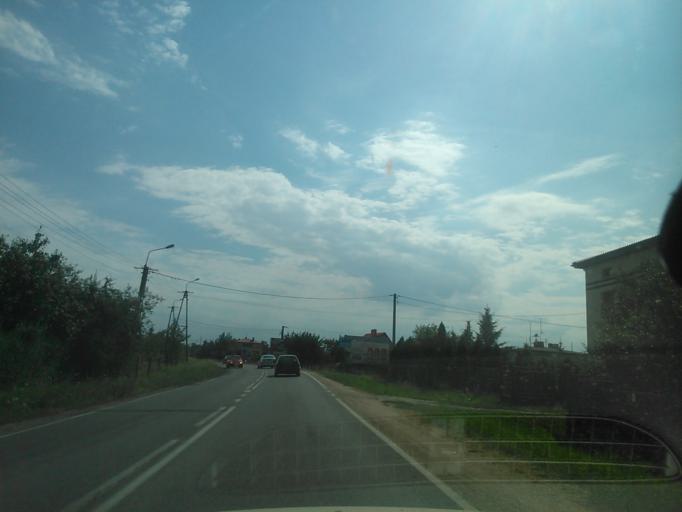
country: PL
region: Masovian Voivodeship
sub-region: Powiat mlawski
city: Mlawa
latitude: 53.1331
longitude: 20.3434
